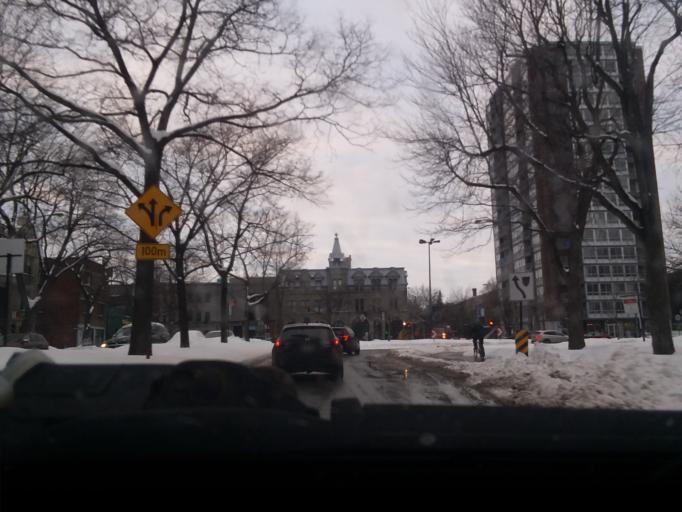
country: CA
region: Quebec
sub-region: Montreal
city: Montreal
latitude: 45.5252
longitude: -73.5735
